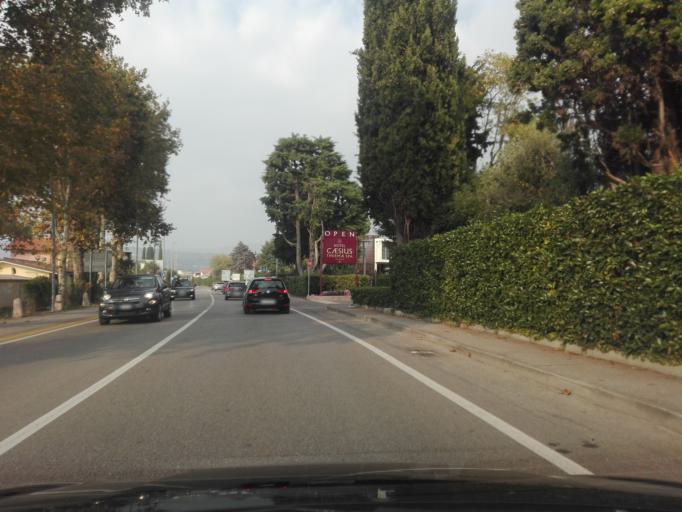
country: IT
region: Veneto
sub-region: Provincia di Verona
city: Bardolino
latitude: 45.5345
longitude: 10.7274
